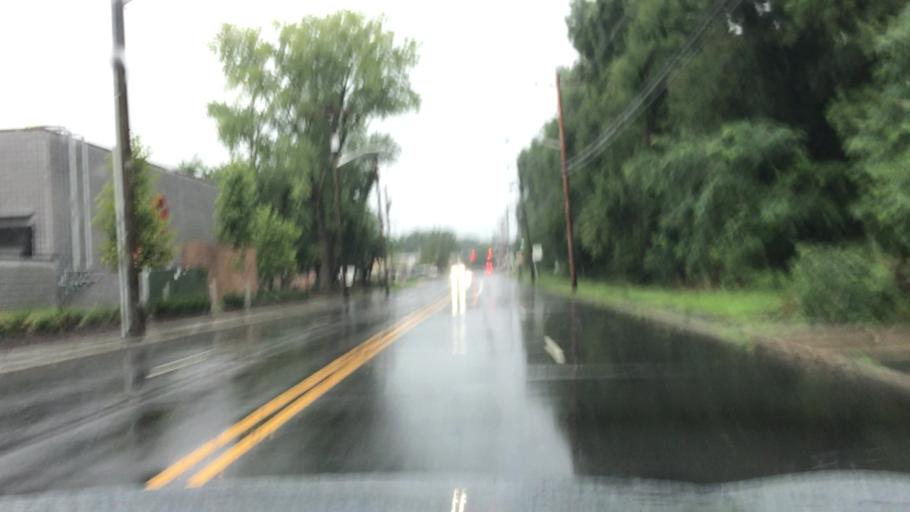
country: US
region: New Jersey
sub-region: Bergen County
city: Closter
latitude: 40.9717
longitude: -73.9569
